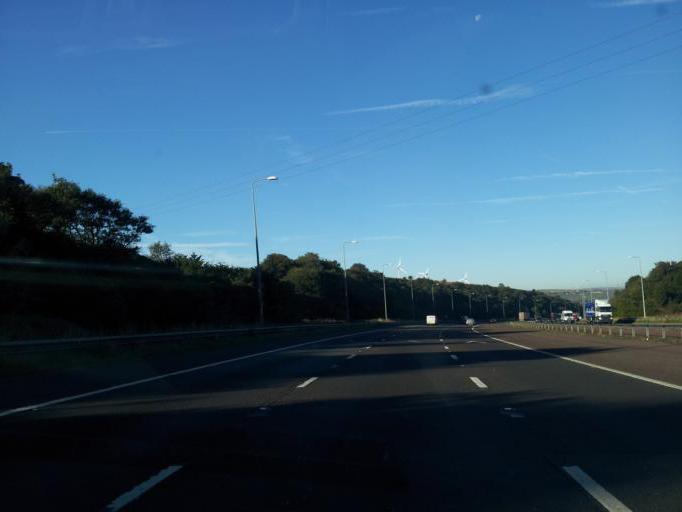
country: GB
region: England
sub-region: Kirklees
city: Marsden
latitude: 53.6444
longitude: -1.8960
